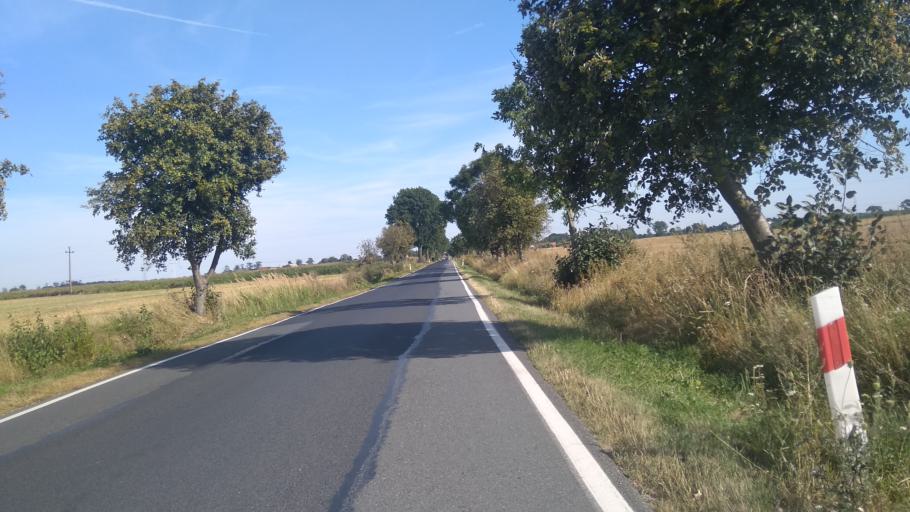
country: PL
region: Kujawsko-Pomorskie
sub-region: Powiat bydgoski
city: Osielsko
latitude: 53.2170
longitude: 18.1412
